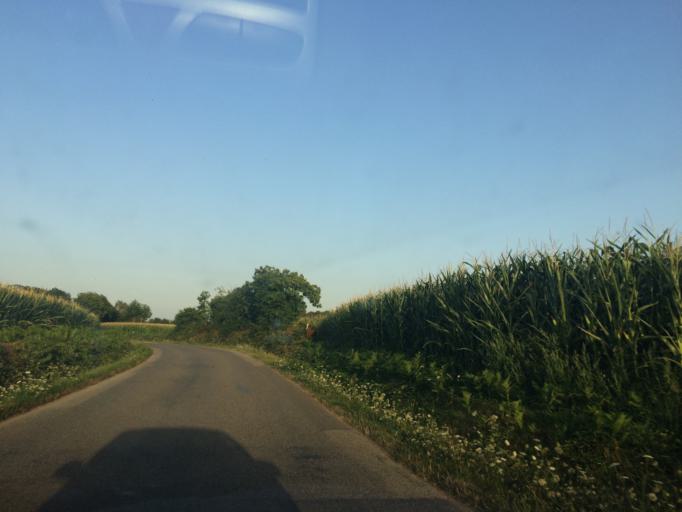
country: FR
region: Brittany
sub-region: Departement du Morbihan
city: Beganne
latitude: 47.6369
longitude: -2.2289
